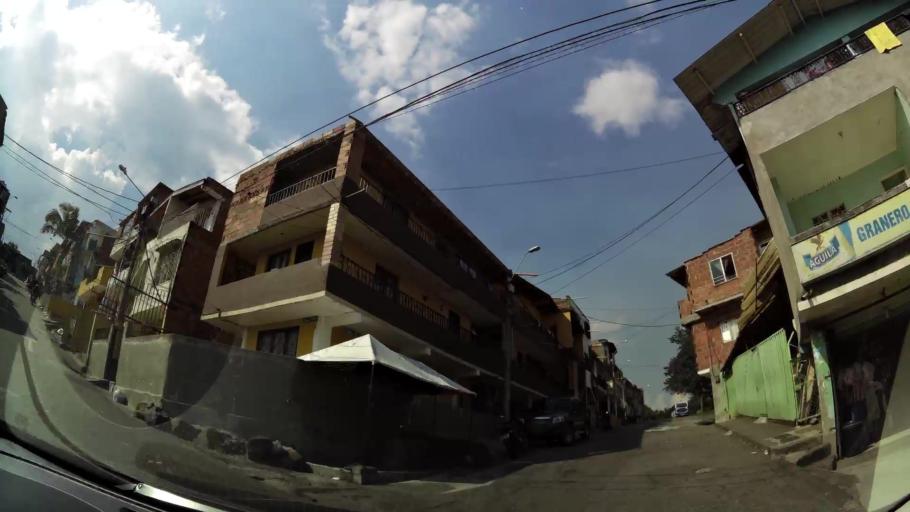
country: CO
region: Antioquia
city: Medellin
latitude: 6.2855
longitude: -75.5927
